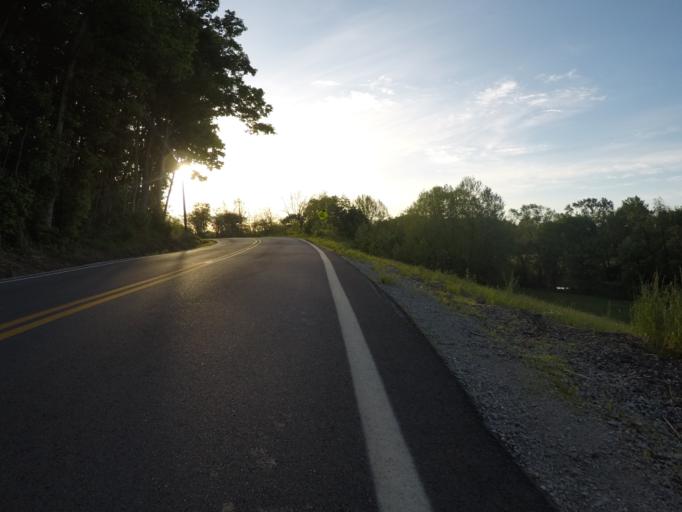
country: US
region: West Virginia
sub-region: Cabell County
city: Huntington
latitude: 38.5233
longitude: -82.4651
